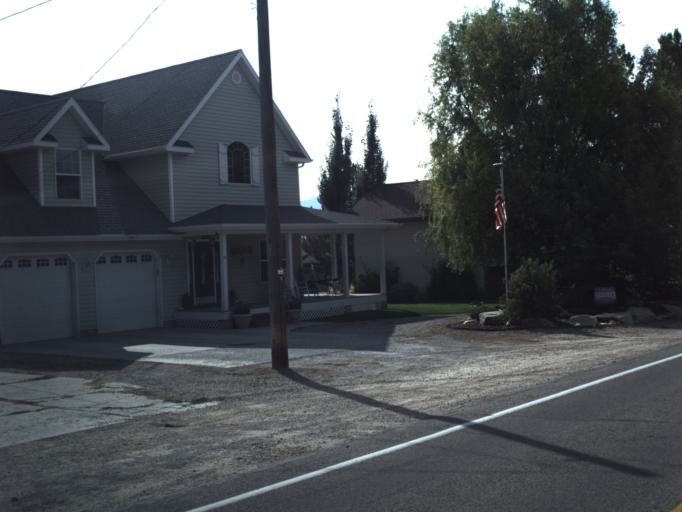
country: US
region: Utah
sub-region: Wasatch County
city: Midway
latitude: 40.5112
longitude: -111.4723
